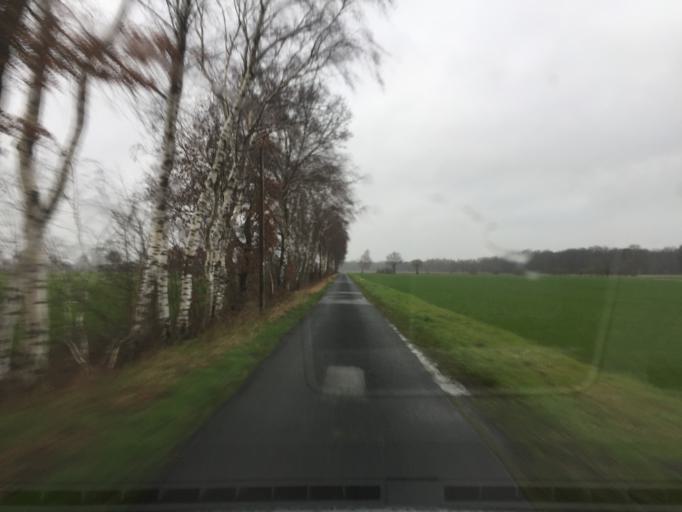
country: DE
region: Lower Saxony
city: Borstel
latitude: 52.6182
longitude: 8.9289
